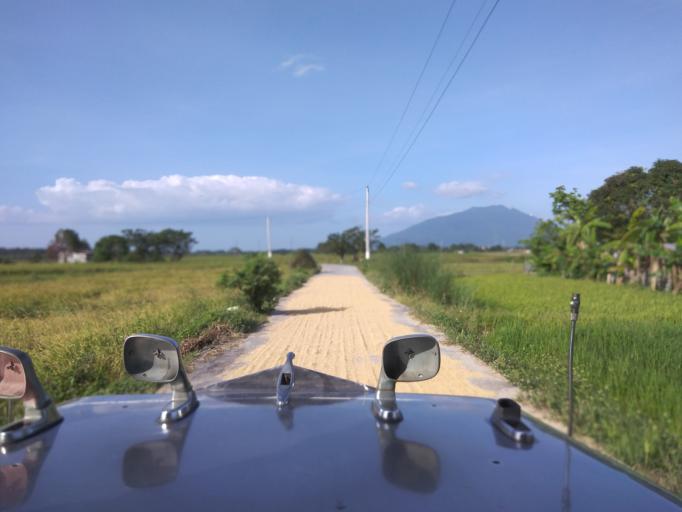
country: PH
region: Central Luzon
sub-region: Province of Pampanga
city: Malino
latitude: 15.0993
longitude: 120.6945
